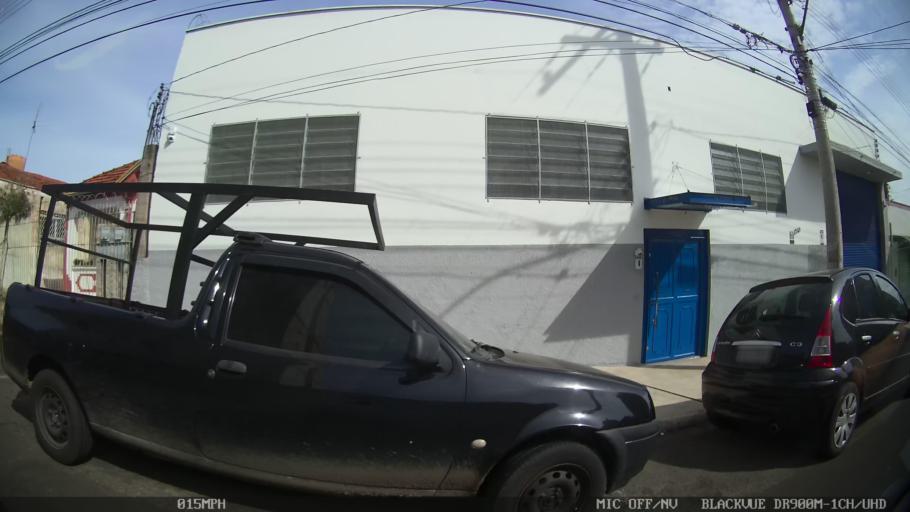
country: BR
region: Sao Paulo
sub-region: Piracicaba
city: Piracicaba
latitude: -22.7493
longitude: -47.6486
